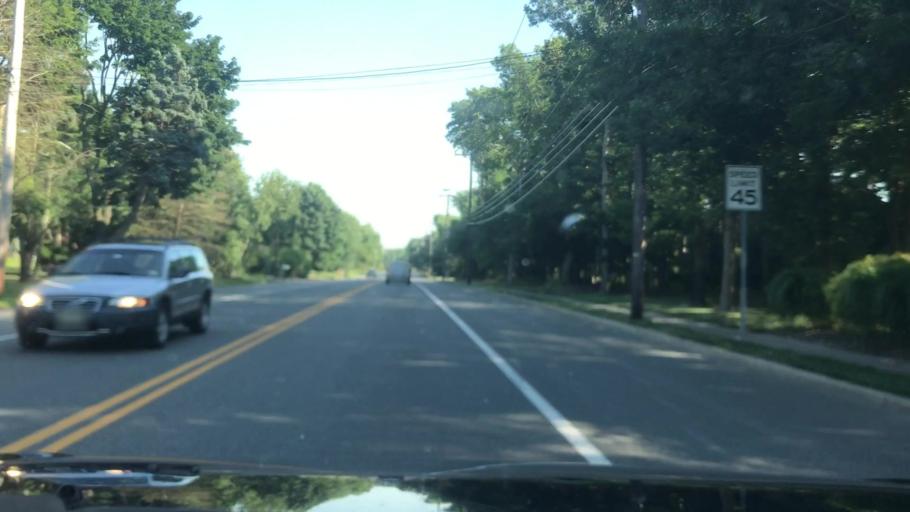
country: US
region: New Jersey
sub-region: Ocean County
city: Leisure Village
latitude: 40.0268
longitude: -74.2011
